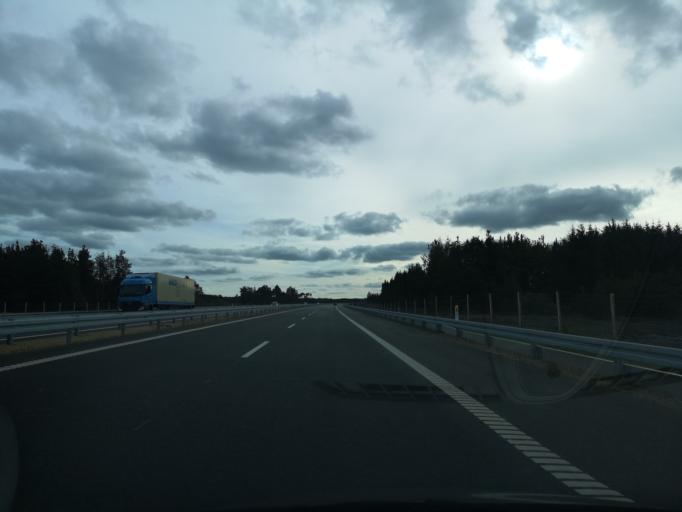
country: DK
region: Central Jutland
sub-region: Herning Kommune
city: Avlum
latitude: 56.3367
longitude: 8.7374
